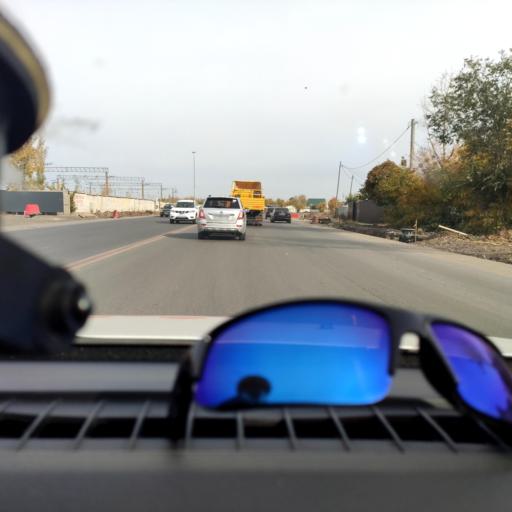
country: RU
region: Samara
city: Samara
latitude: 53.1270
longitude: 50.0903
